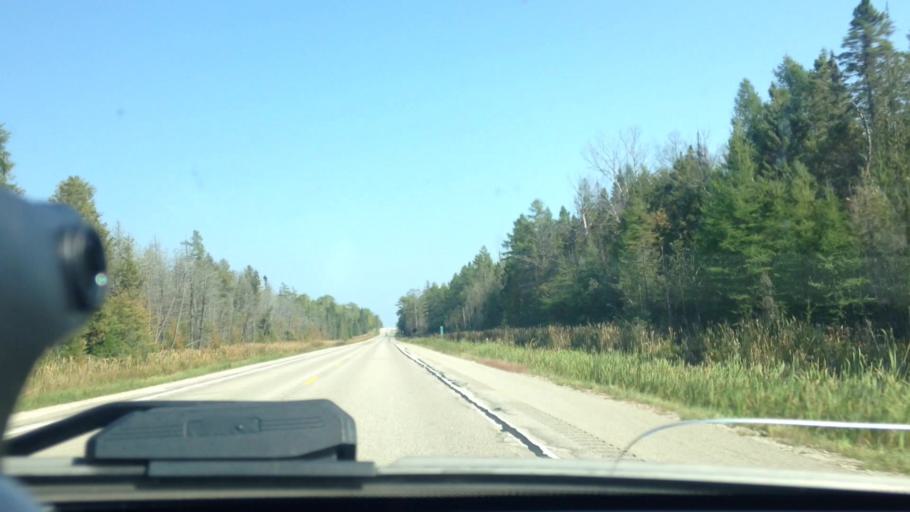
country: US
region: Michigan
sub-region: Luce County
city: Newberry
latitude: 46.3036
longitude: -85.3054
